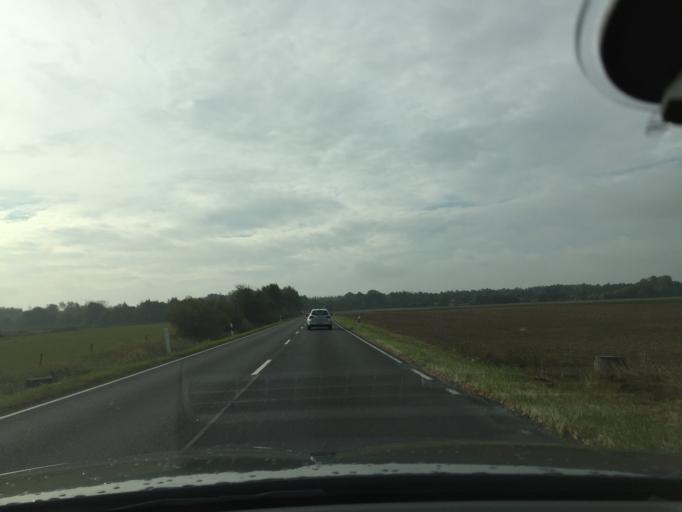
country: DE
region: Mecklenburg-Vorpommern
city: Ostseebad Dierhagen
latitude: 54.2279
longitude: 12.3655
